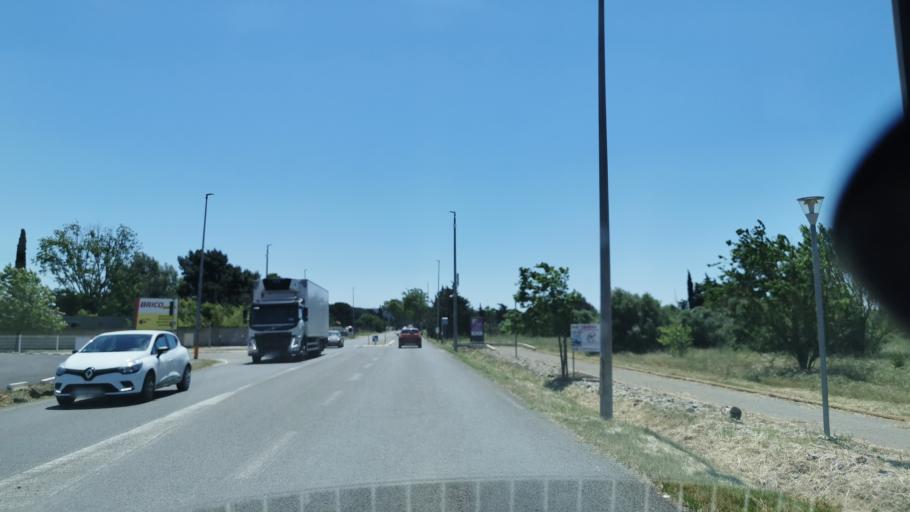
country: FR
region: Languedoc-Roussillon
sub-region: Departement de l'Aude
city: Saint-Marcel-sur-Aude
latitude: 43.2538
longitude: 2.9126
